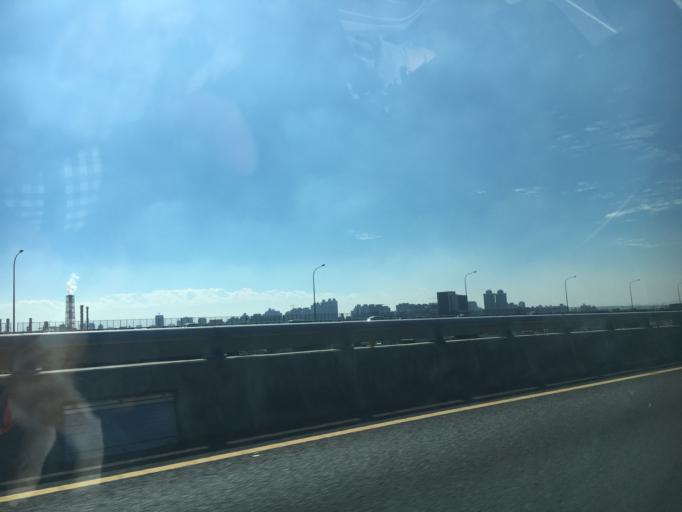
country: TW
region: Taiwan
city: Taoyuan City
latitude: 25.0424
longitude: 121.3054
